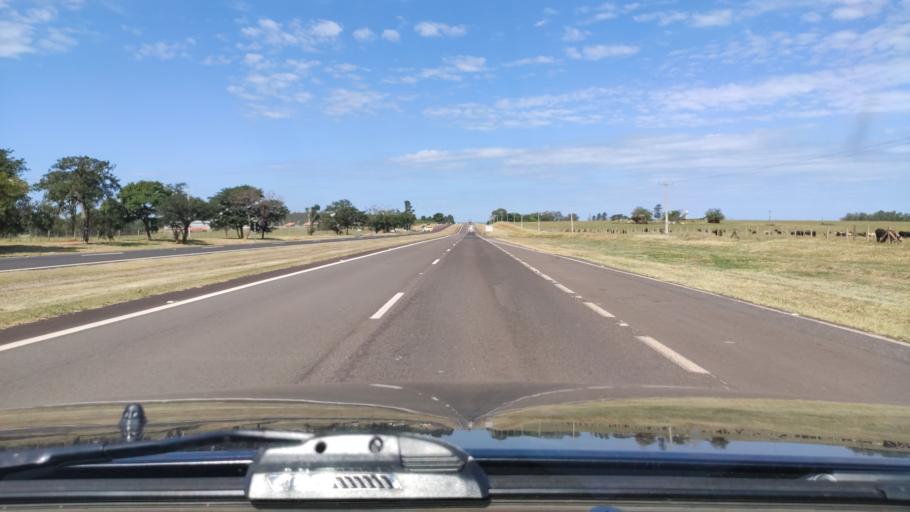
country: BR
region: Sao Paulo
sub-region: Rancharia
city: Rancharia
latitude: -22.4510
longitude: -50.9816
